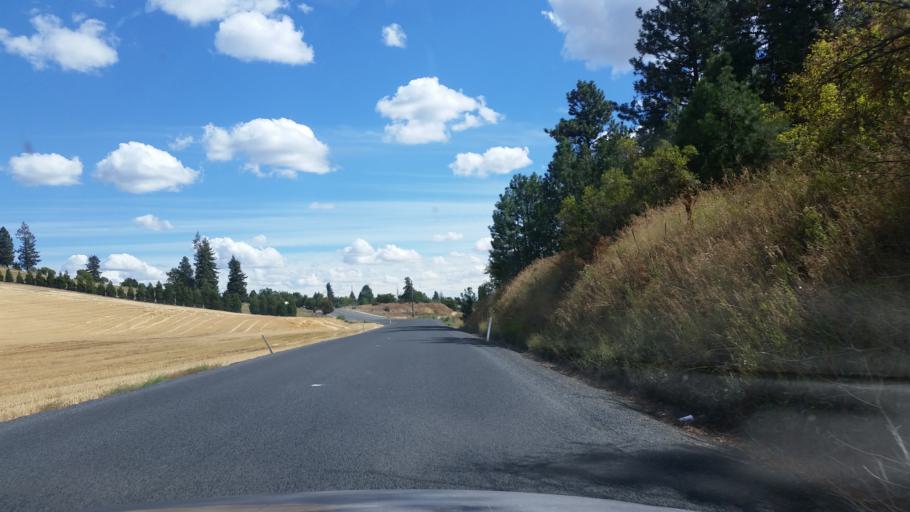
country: US
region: Washington
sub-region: Spokane County
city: Cheney
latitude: 47.4826
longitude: -117.6087
